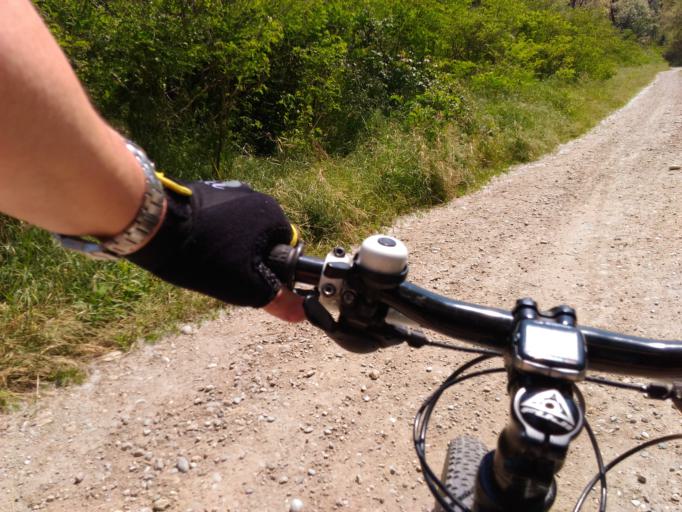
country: IT
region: Lombardy
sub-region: Provincia di Lodi
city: Montanaso Lombardo
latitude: 45.3527
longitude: 9.4719
